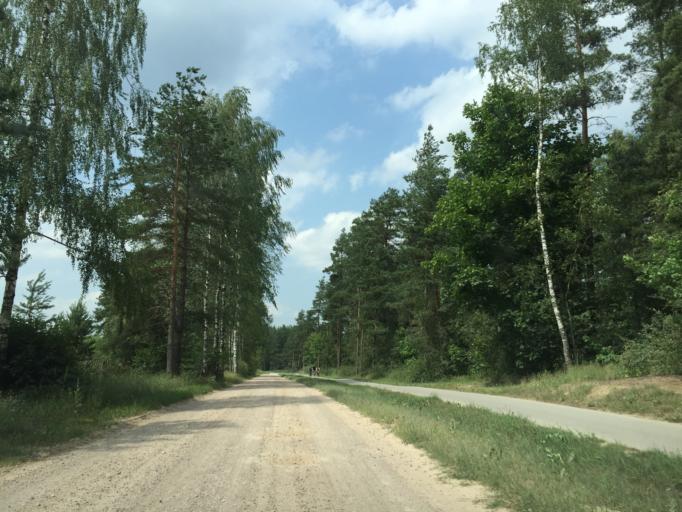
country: LV
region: Olaine
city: Olaine
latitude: 56.7774
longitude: 23.9016
